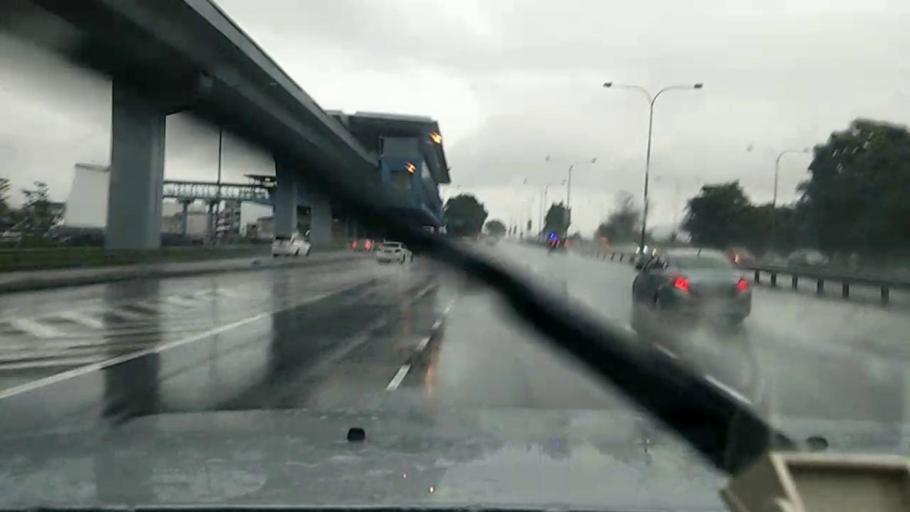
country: MY
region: Selangor
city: Kampong Baharu Balakong
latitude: 3.0392
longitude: 101.7729
